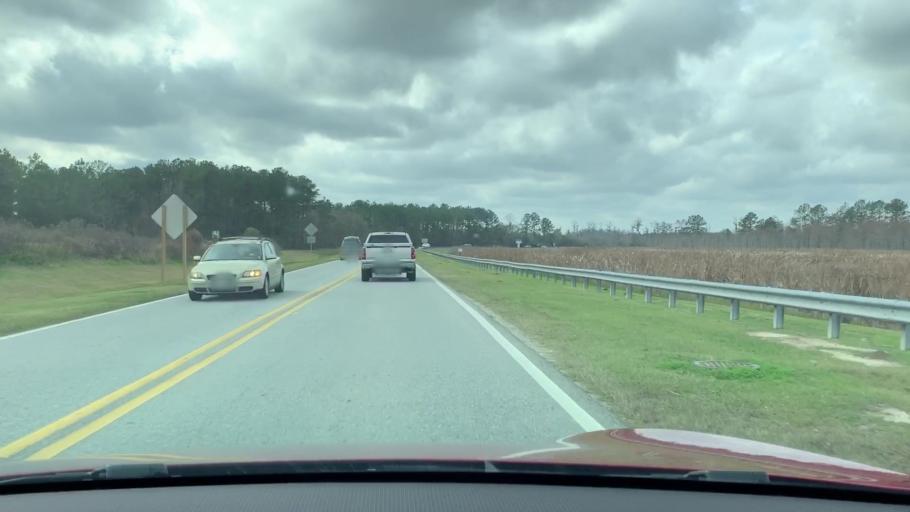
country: US
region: Georgia
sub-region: Chatham County
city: Pooler
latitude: 32.1409
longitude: -81.2113
